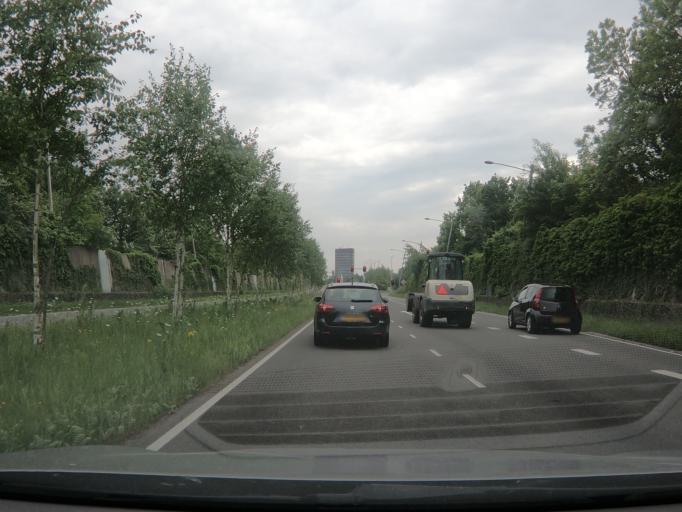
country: NL
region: Drenthe
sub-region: Gemeente Assen
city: Assen
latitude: 52.9998
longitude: 6.5354
